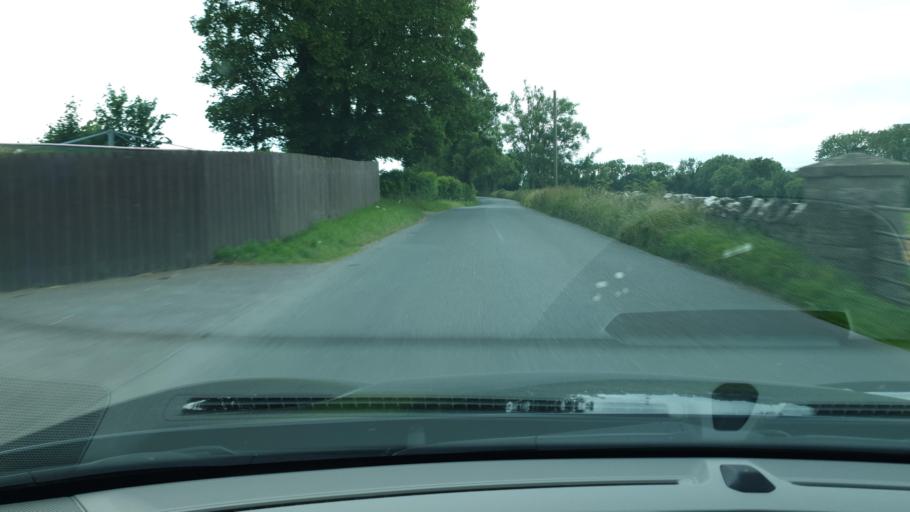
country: IE
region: Leinster
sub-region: An Mhi
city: Ratoath
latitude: 53.5379
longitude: -6.4353
